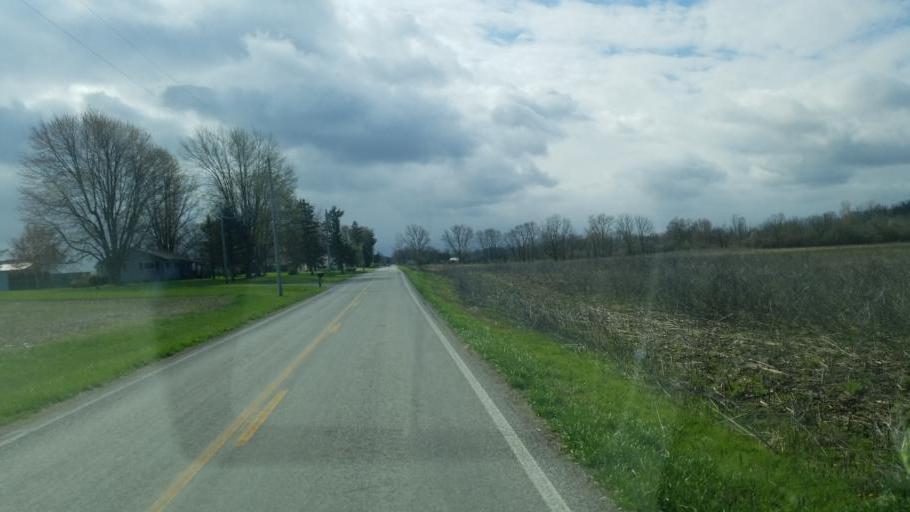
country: US
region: Ohio
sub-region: Delaware County
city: Ashley
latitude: 40.3803
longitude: -83.0355
